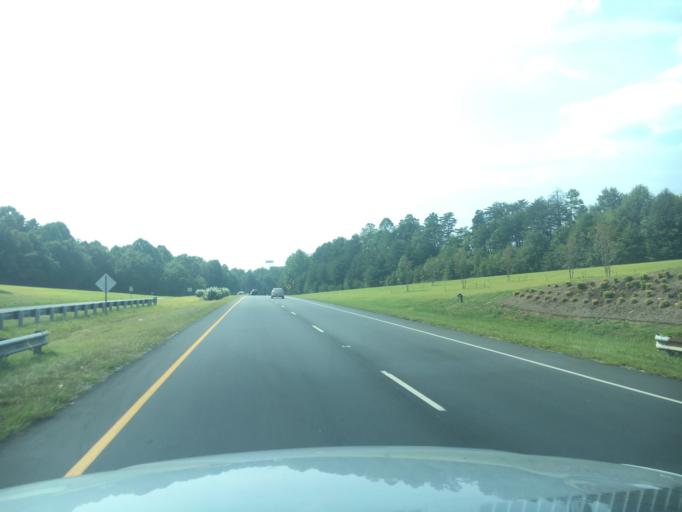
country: US
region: North Carolina
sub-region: Rutherford County
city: Spindale
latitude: 35.3422
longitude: -81.9193
